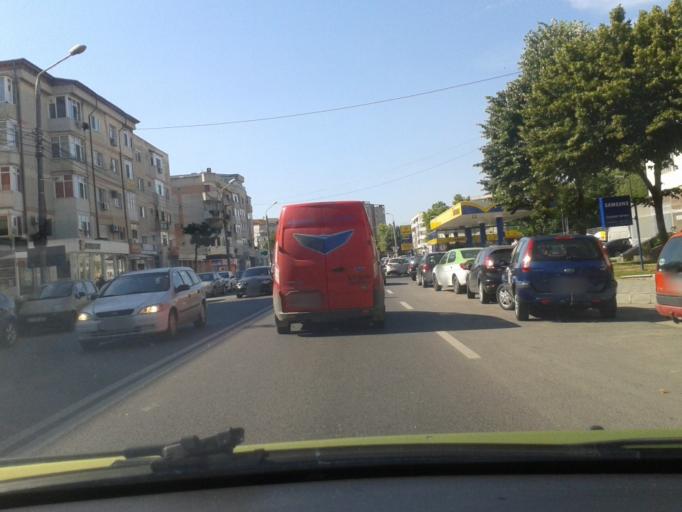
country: RO
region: Constanta
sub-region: Municipiul Mangalia
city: Mangalia
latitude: 43.8190
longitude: 28.5831
